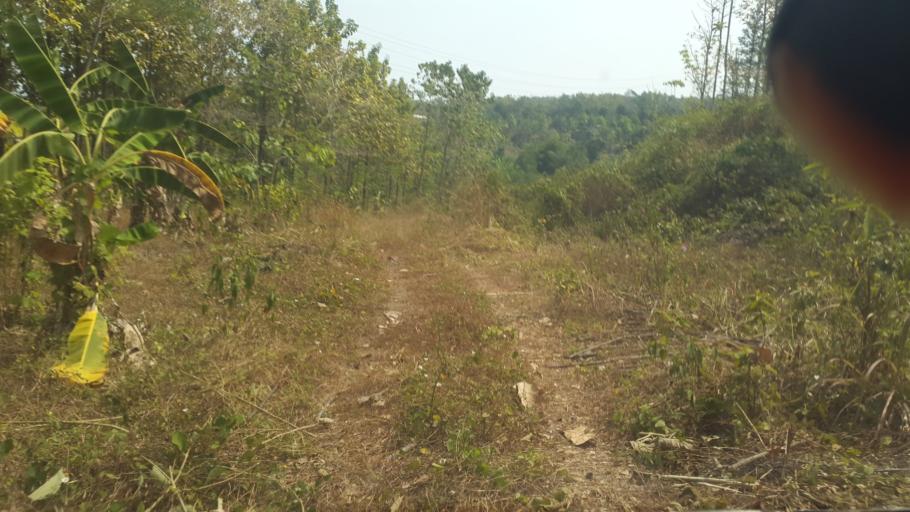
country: ID
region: West Java
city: Cimaja
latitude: -6.9468
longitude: 106.5042
